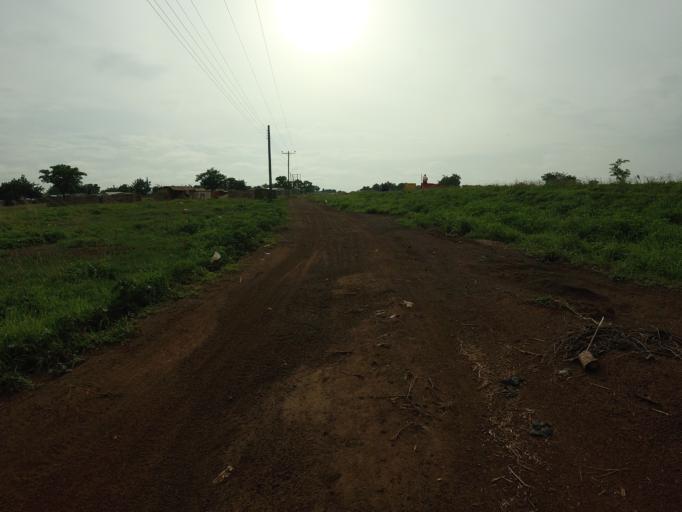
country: GH
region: Northern
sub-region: Yendi
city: Yendi
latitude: 9.9315
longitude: -0.2047
